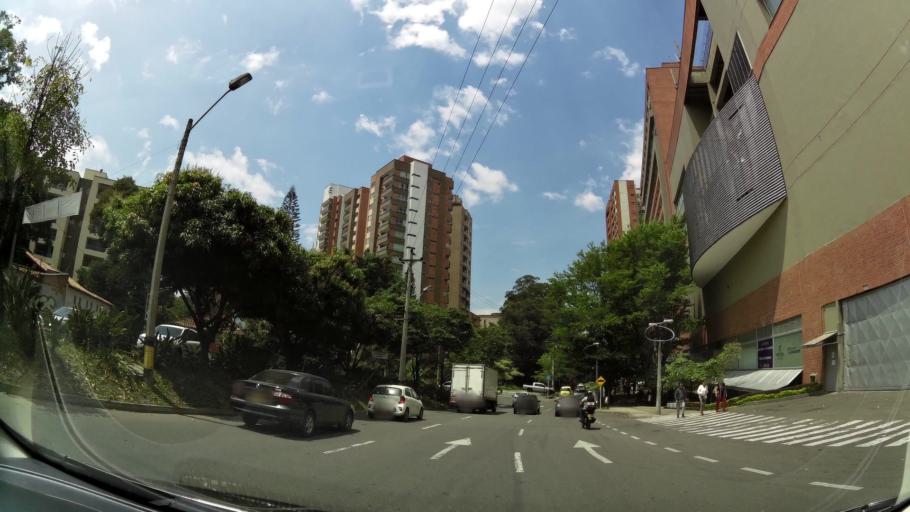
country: CO
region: Antioquia
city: Envigado
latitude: 6.1843
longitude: -75.5798
